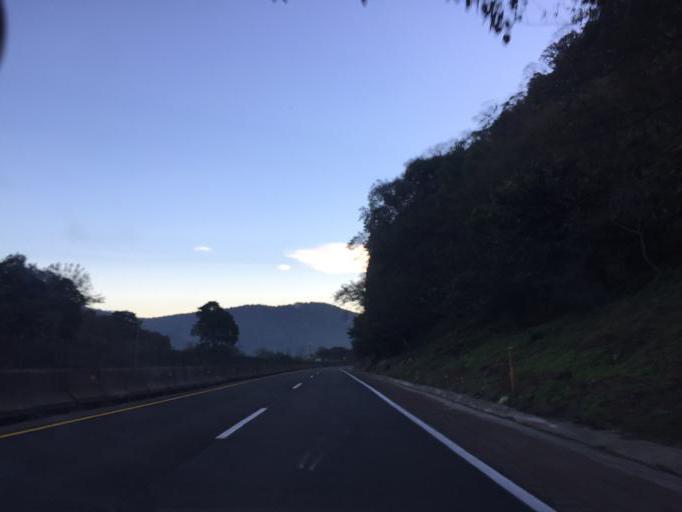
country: MX
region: Veracruz
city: Nogales
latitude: 18.8314
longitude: -97.1445
